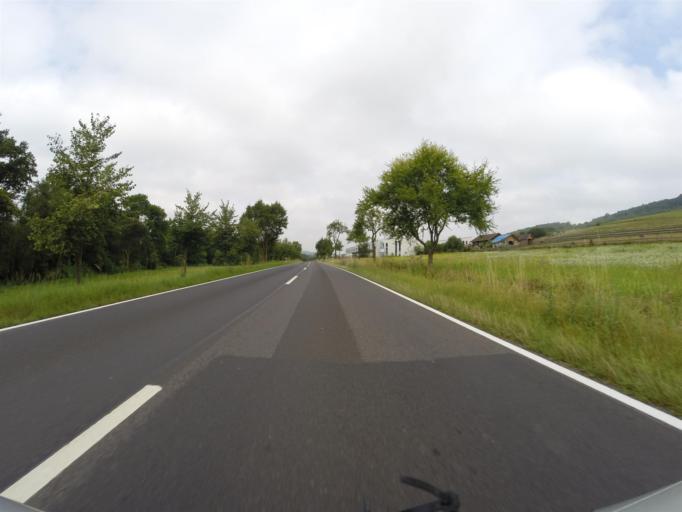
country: DE
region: Thuringia
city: Ifta
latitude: 51.0574
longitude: 10.1947
